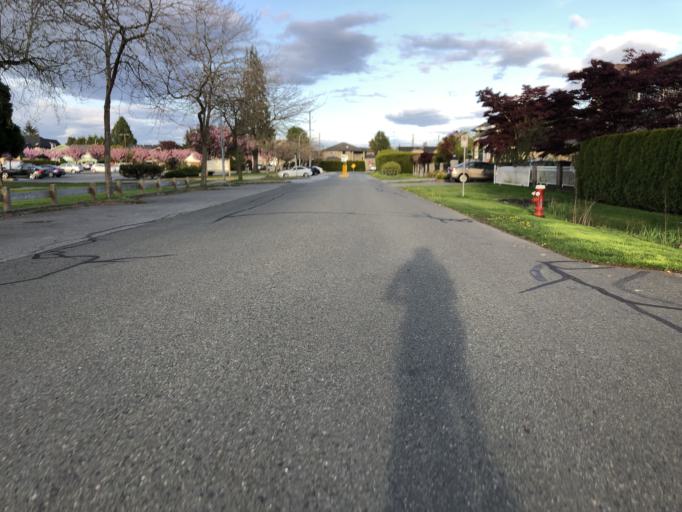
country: CA
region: British Columbia
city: Richmond
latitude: 49.1416
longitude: -123.1110
